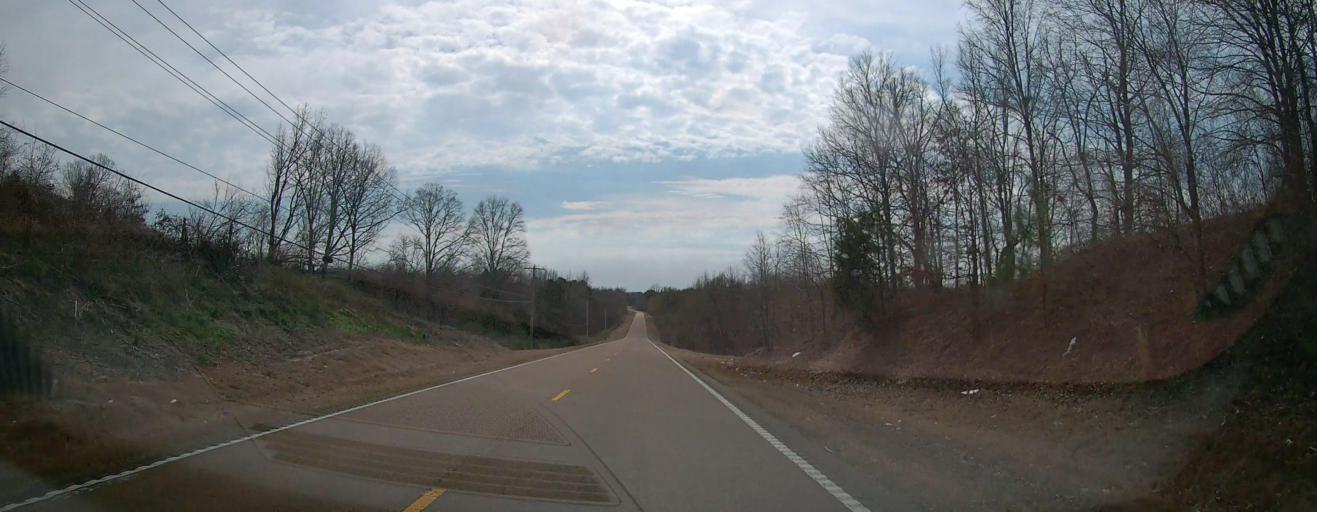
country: US
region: Mississippi
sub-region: Marshall County
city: Holly Springs
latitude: 34.7343
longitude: -89.4218
